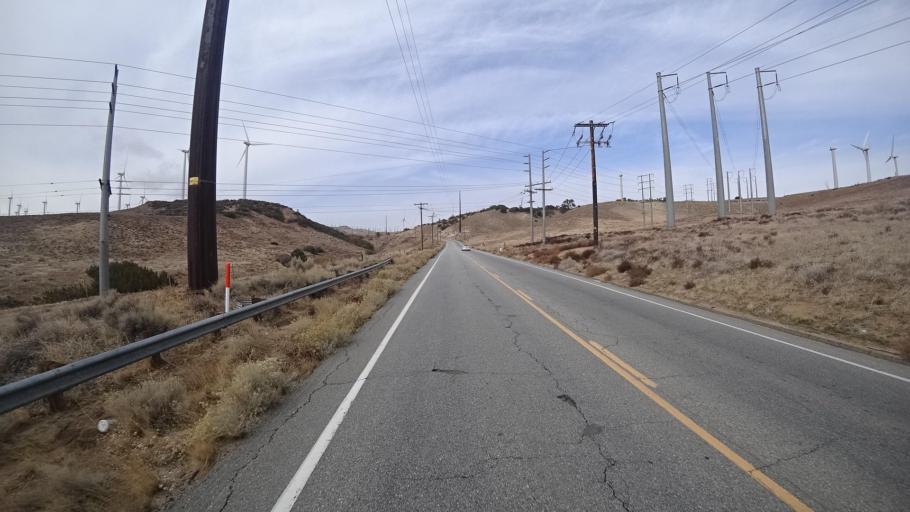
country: US
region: California
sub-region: Kern County
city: Tehachapi
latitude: 35.0538
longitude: -118.3640
